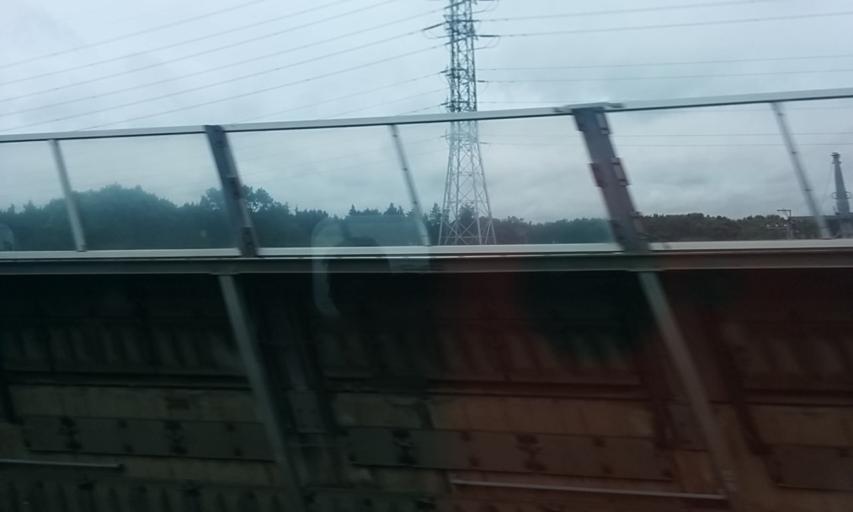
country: JP
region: Tochigi
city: Oyama
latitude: 36.2745
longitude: 139.7764
